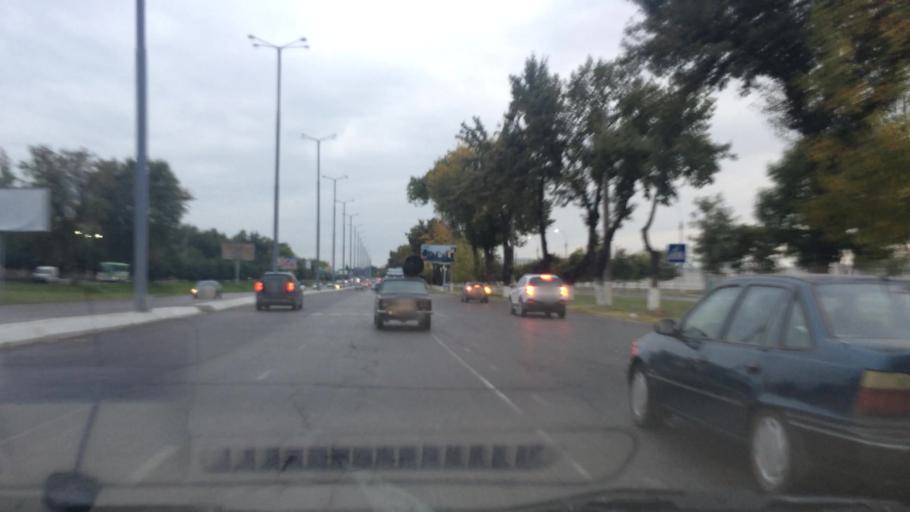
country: UZ
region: Toshkent Shahri
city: Tashkent
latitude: 41.2506
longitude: 69.1834
